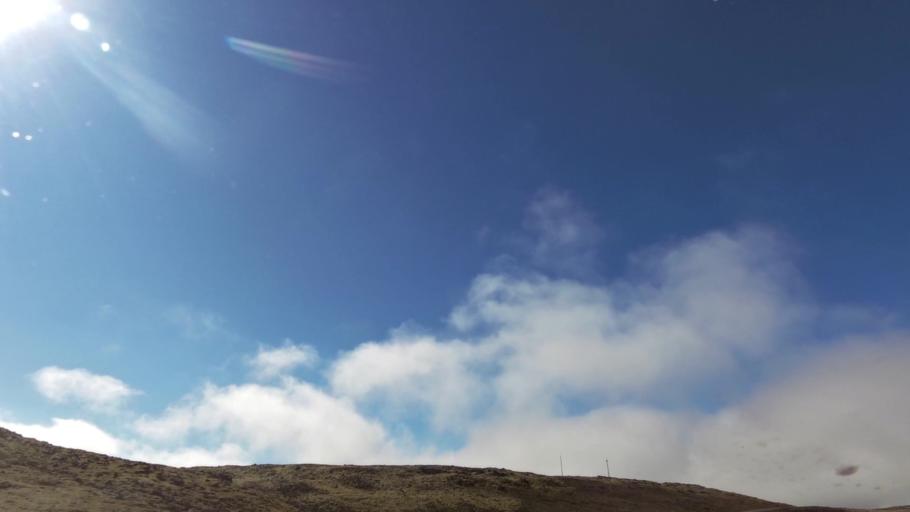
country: IS
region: West
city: Olafsvik
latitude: 65.5534
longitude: -24.2255
